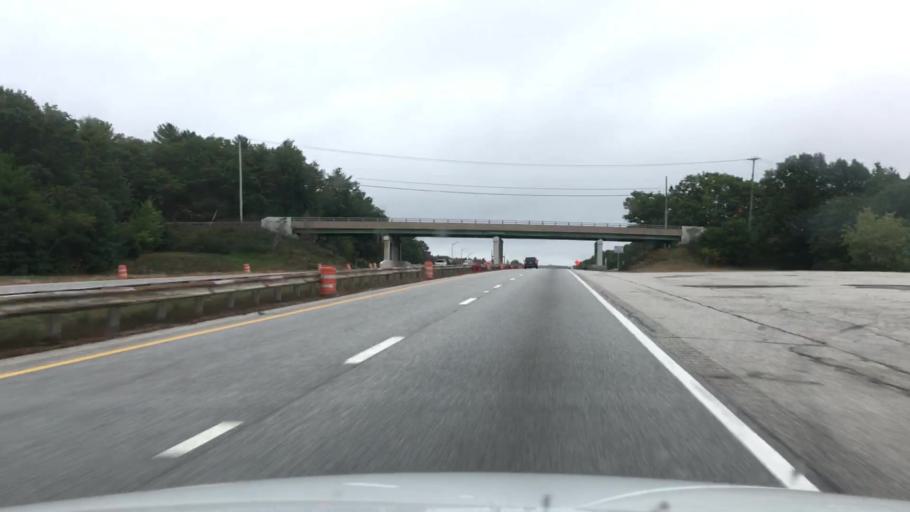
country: US
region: Maine
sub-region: Cumberland County
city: Cumberland Center
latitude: 43.8131
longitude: -70.3175
